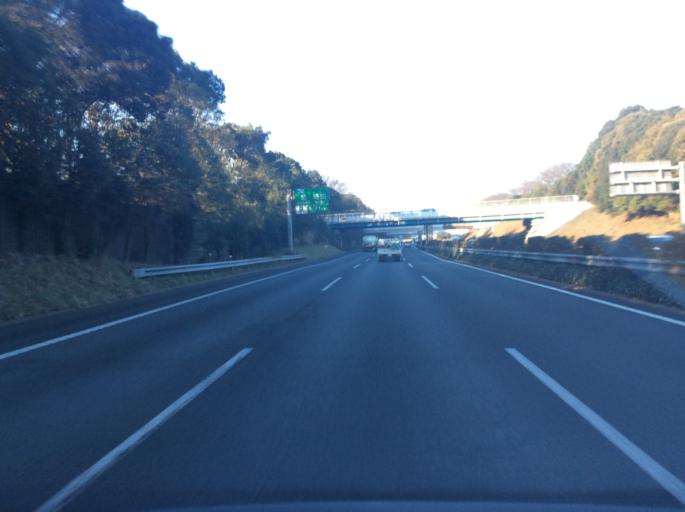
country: JP
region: Ibaraki
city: Moriya
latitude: 35.9155
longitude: 139.9484
